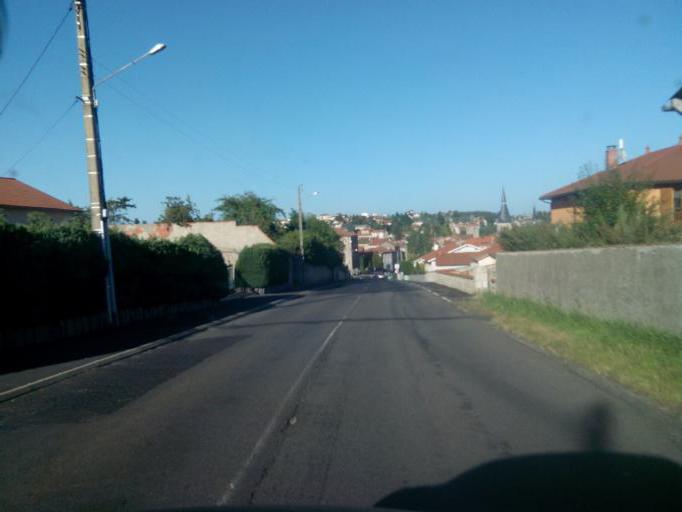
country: FR
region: Auvergne
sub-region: Departement de la Haute-Loire
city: Craponne-sur-Arzon
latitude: 45.3299
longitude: 3.8416
